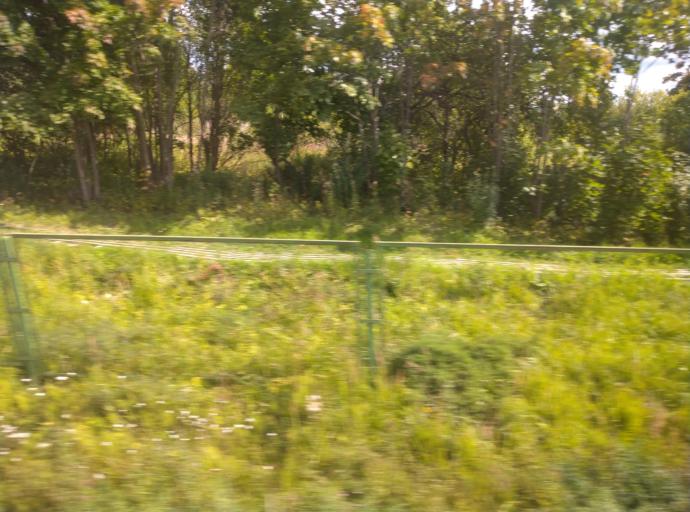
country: RU
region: Leningrad
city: Krasnyy Bor
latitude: 59.6831
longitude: 30.6971
